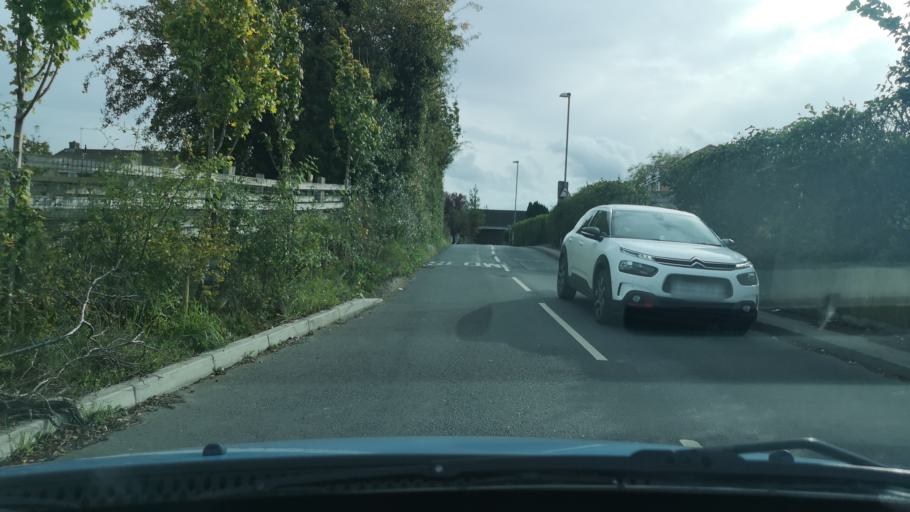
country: GB
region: England
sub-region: City and Borough of Wakefield
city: Normanton
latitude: 53.6897
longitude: -1.3995
